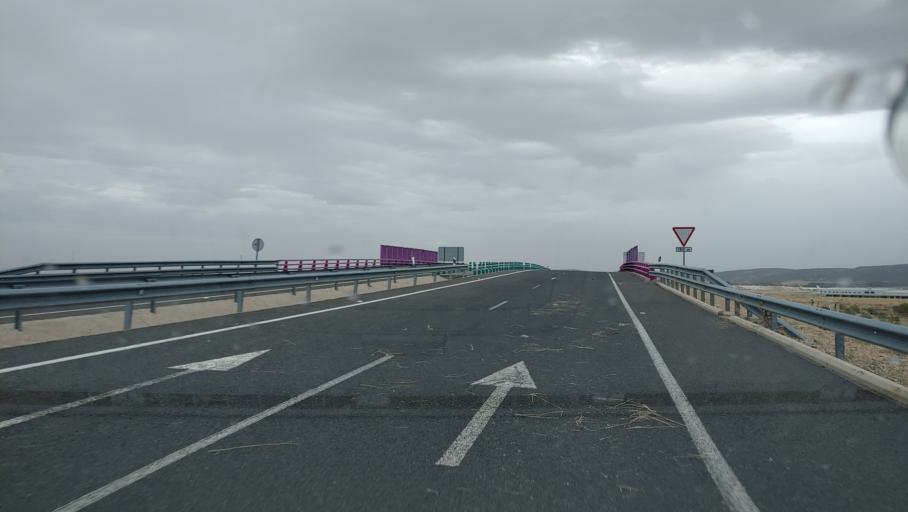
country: ES
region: Castille-La Mancha
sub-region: Provincia de Ciudad Real
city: Canada de Calatrava
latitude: 38.8730
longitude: -3.9923
